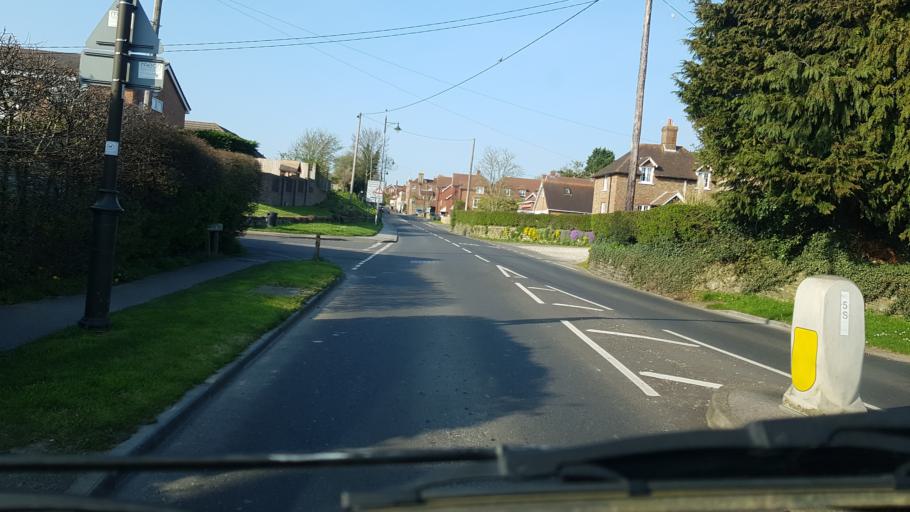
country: GB
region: England
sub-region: West Sussex
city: Petworth
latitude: 50.9824
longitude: -0.6116
